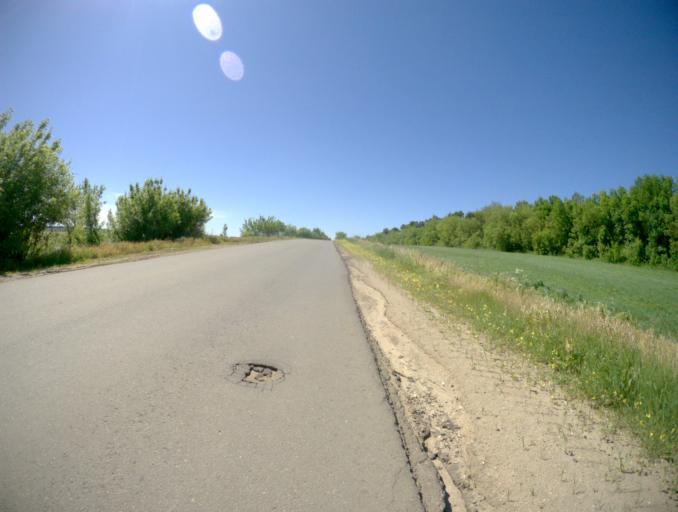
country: RU
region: Ivanovo
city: Gavrilov Posad
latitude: 56.5649
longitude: 40.0234
